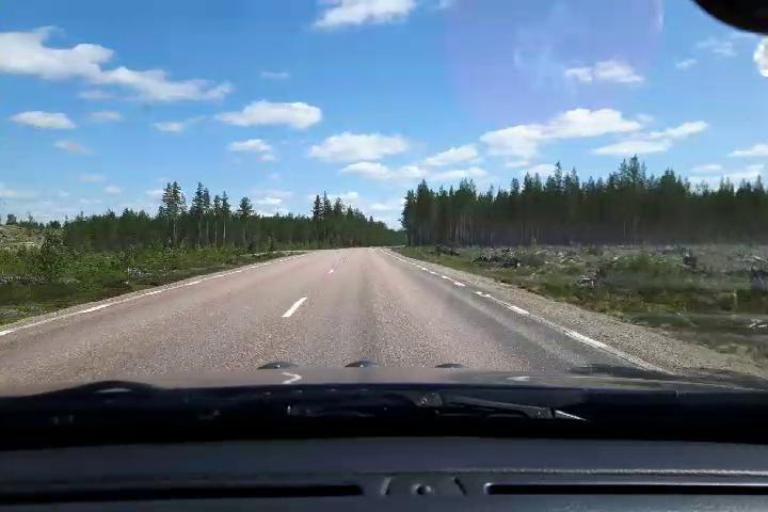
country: SE
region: Gaevleborg
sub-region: Ljusdals Kommun
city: Farila
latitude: 61.9416
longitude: 15.4751
